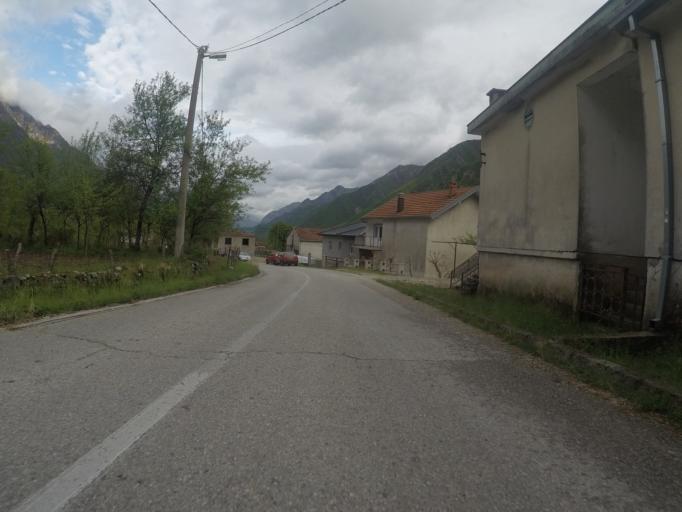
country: BA
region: Federation of Bosnia and Herzegovina
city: Siroki Brijeg
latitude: 43.5419
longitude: 17.5618
